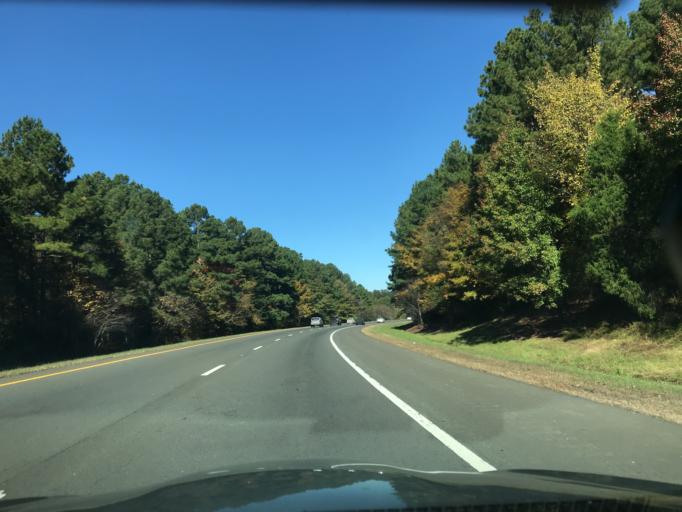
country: US
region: North Carolina
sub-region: Wake County
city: Morrisville
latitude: 35.9007
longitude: -78.8703
